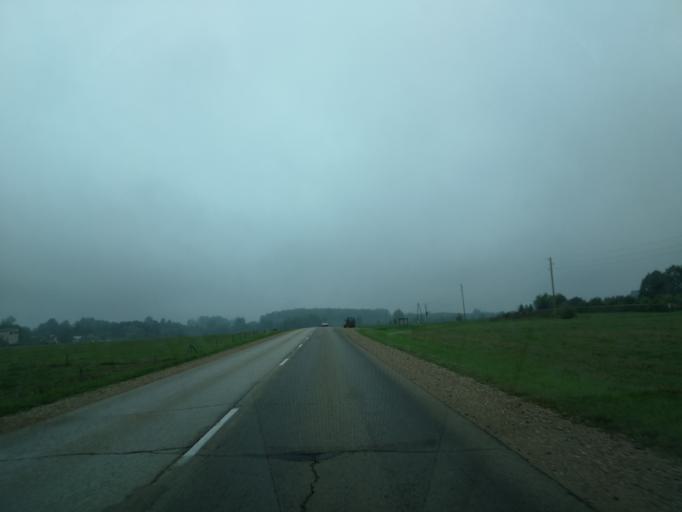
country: LV
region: Preilu Rajons
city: Preili
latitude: 56.2984
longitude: 26.6633
